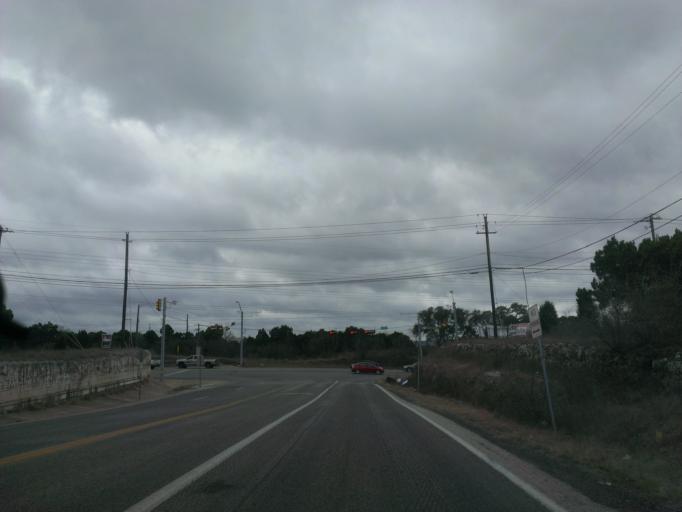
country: US
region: Texas
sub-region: Travis County
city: Hudson Bend
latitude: 30.3951
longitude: -97.8695
